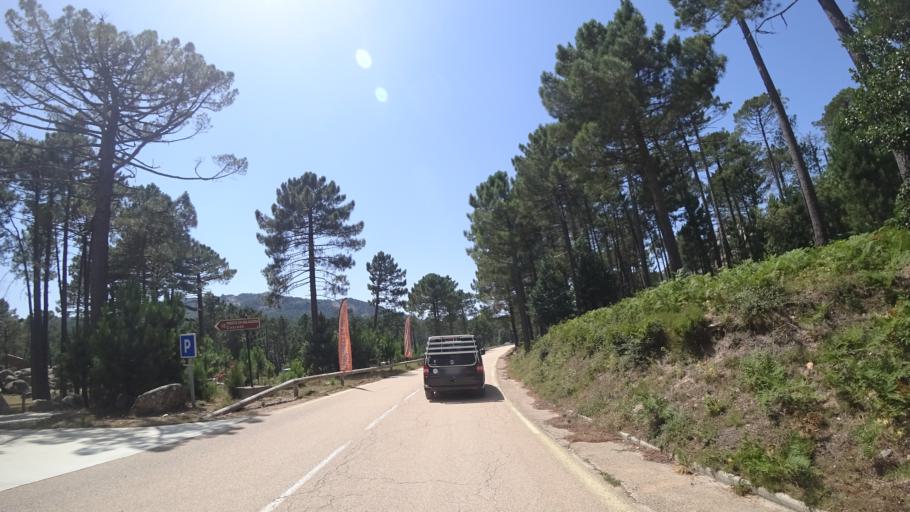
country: FR
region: Corsica
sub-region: Departement de la Corse-du-Sud
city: Zonza
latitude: 41.6881
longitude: 9.2001
